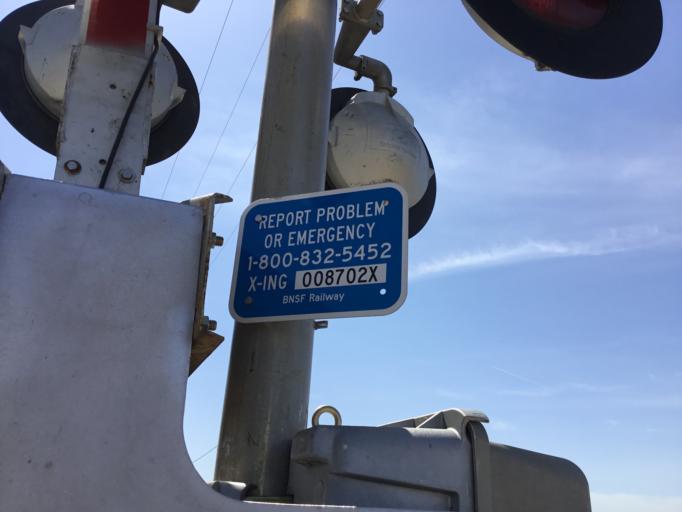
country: US
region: Kansas
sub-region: Lyon County
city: Emporia
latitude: 38.4019
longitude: -96.2628
